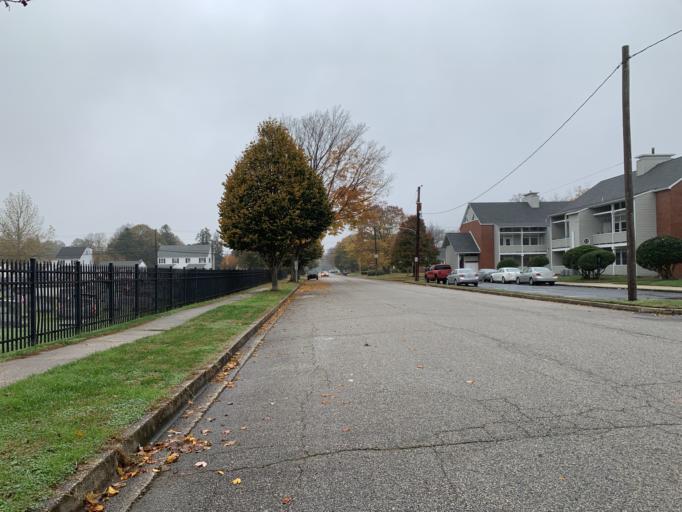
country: US
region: Delaware
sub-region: Kent County
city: Dover
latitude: 39.1672
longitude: -75.5319
